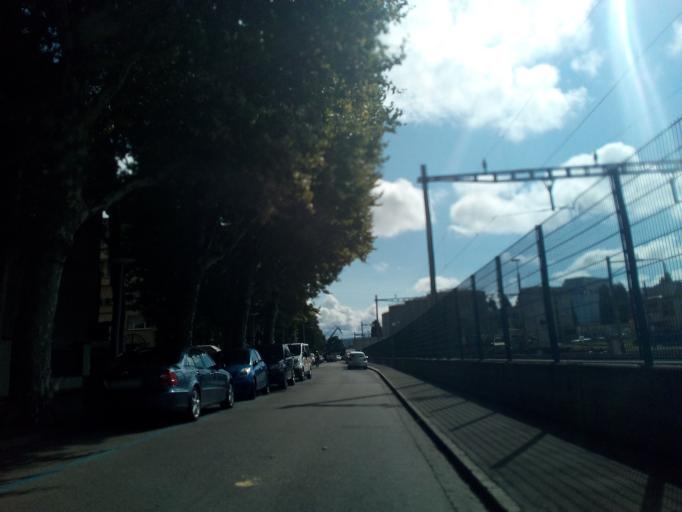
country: FR
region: Alsace
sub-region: Departement du Haut-Rhin
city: Village-Neuf
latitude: 47.5781
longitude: 7.5884
